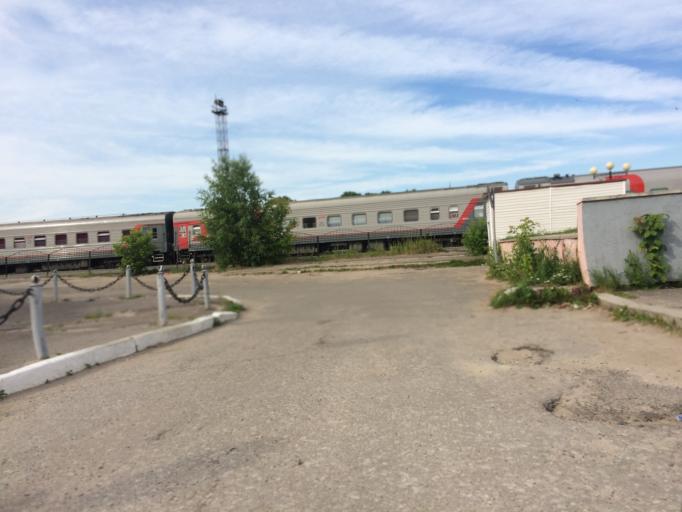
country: RU
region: Mariy-El
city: Yoshkar-Ola
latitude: 56.6205
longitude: 47.8826
